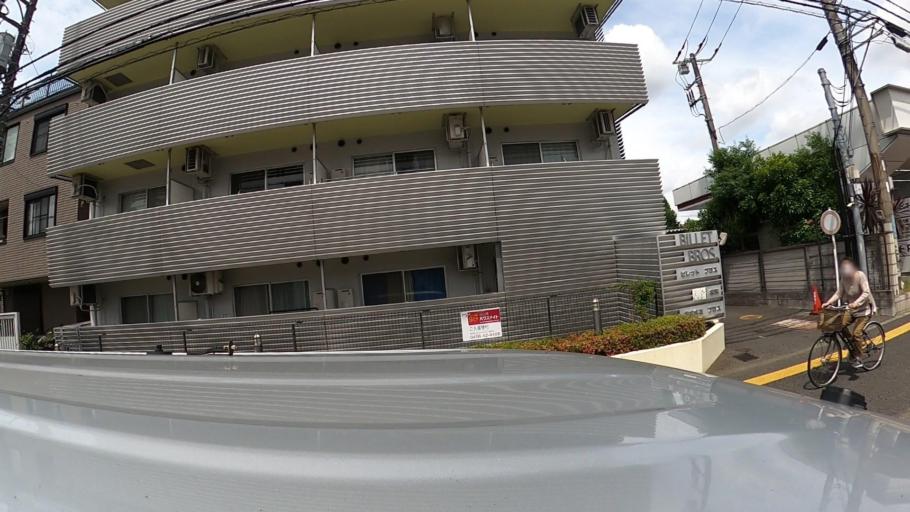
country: JP
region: Kanagawa
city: Fujisawa
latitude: 35.4006
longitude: 139.4696
